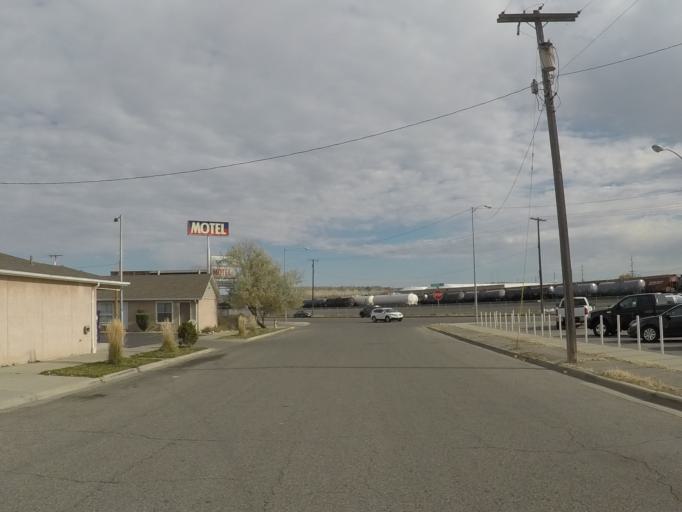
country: US
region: Montana
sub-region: Yellowstone County
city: Billings
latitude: 45.7711
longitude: -108.5270
